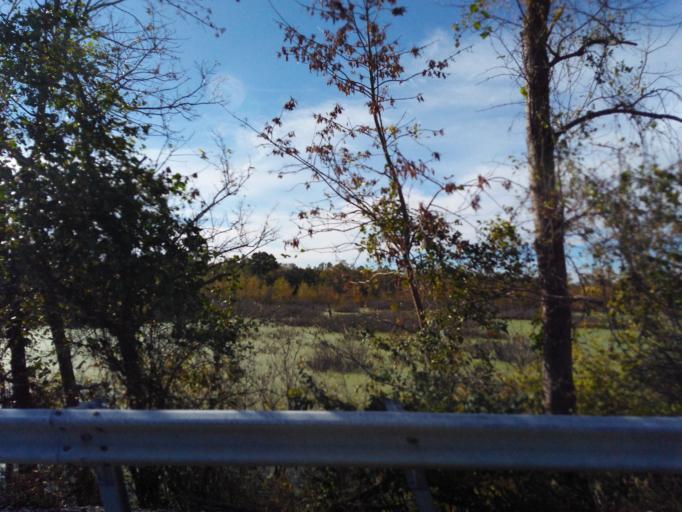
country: US
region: Illinois
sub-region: Madison County
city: Troy
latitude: 38.7167
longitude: -89.8328
